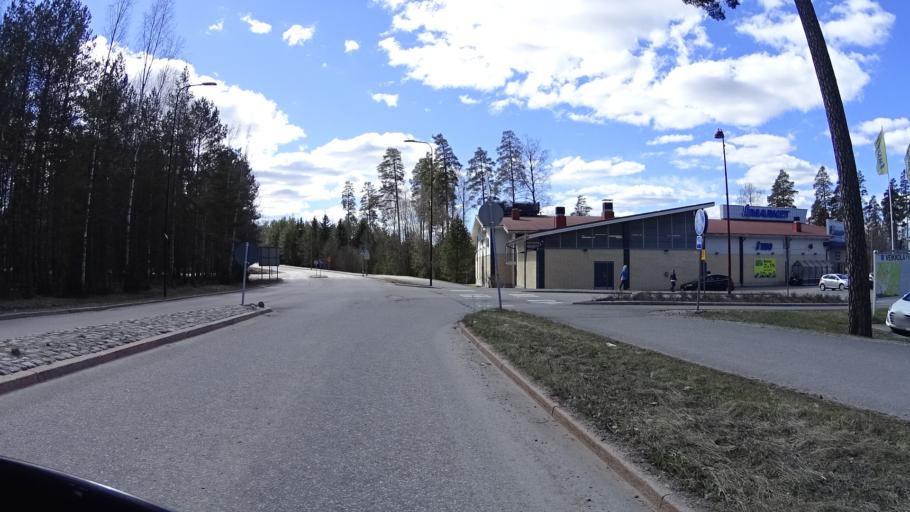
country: FI
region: Uusimaa
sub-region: Helsinki
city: Kirkkonummi
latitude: 60.2691
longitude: 24.4456
